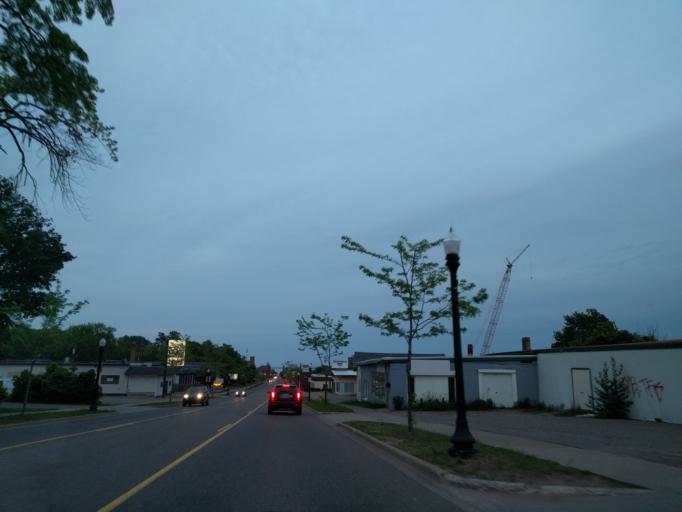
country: US
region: Michigan
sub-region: Marquette County
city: Marquette
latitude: 46.5456
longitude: -87.4089
